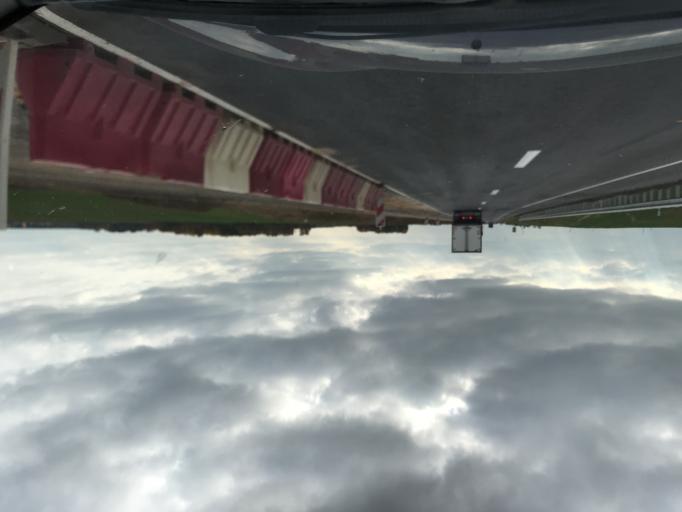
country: BY
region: Grodnenskaya
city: Lida
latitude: 53.8205
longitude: 25.1227
